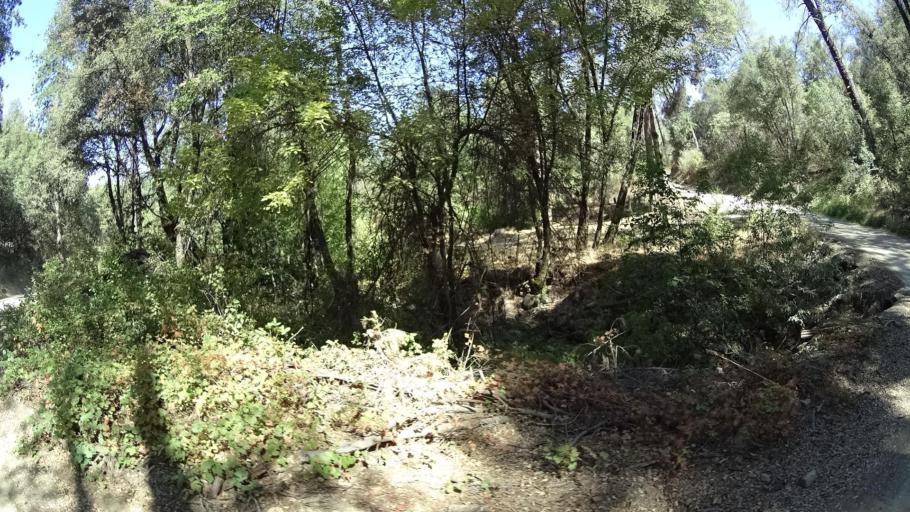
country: US
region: California
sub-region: Madera County
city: Ahwahnee
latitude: 37.4333
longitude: -119.7284
